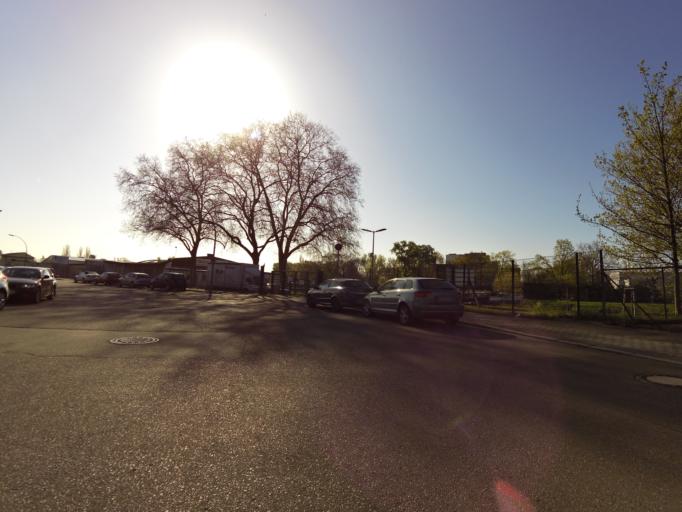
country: DE
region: Berlin
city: Britz
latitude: 52.4602
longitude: 13.4505
